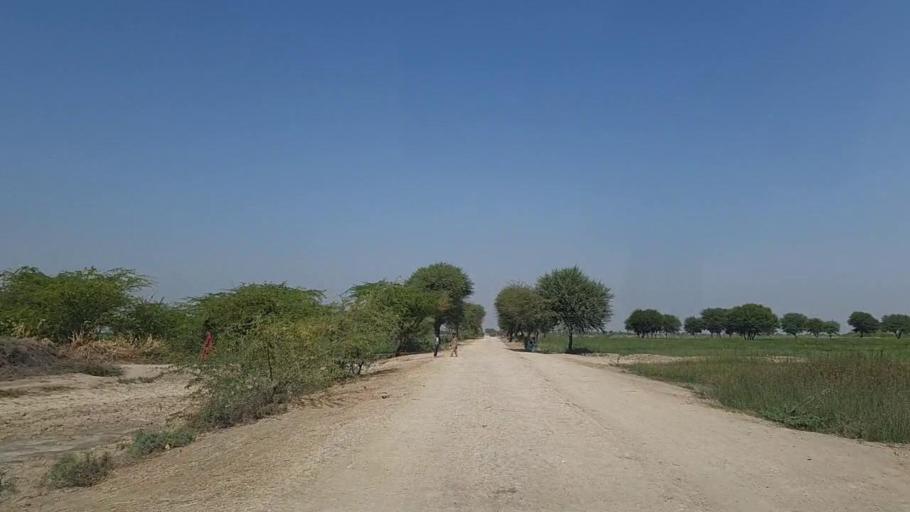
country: PK
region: Sindh
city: Samaro
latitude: 25.1882
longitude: 69.4041
